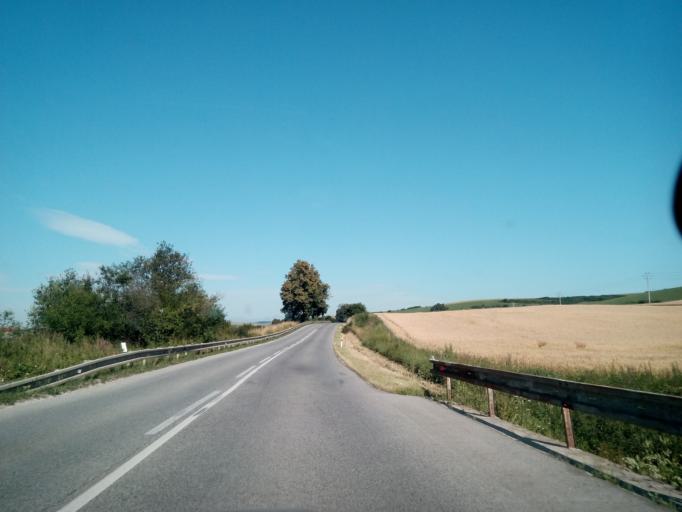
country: SK
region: Kosicky
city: Krompachy
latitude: 48.9422
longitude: 20.8183
